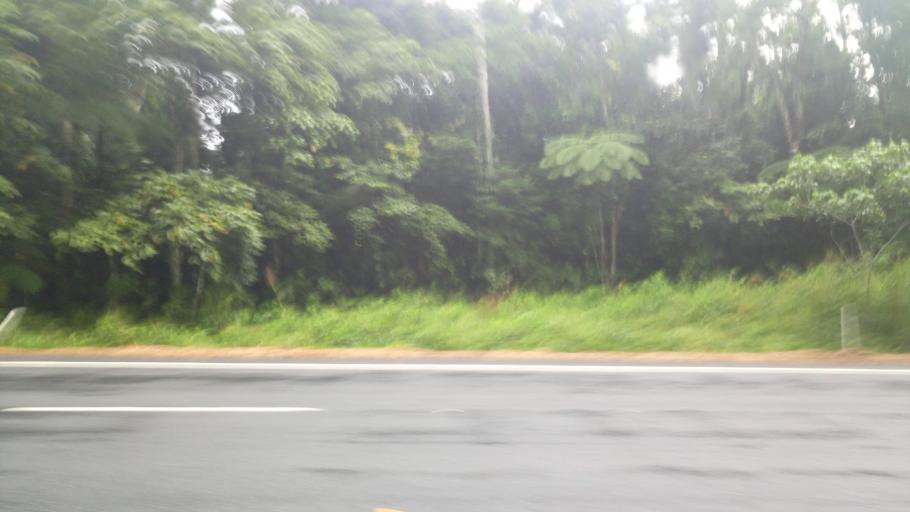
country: AU
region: Queensland
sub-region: Tablelands
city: Ravenshoe
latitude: -17.5956
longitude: 145.7534
